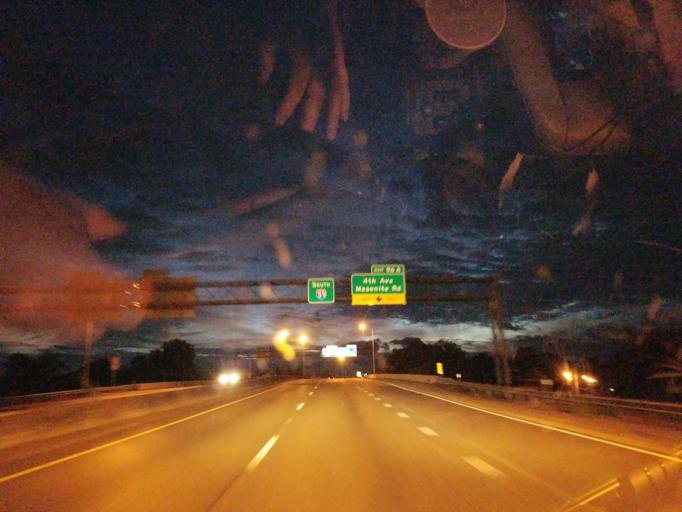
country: US
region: Mississippi
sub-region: Jones County
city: Laurel
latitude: 31.6872
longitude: -89.1241
